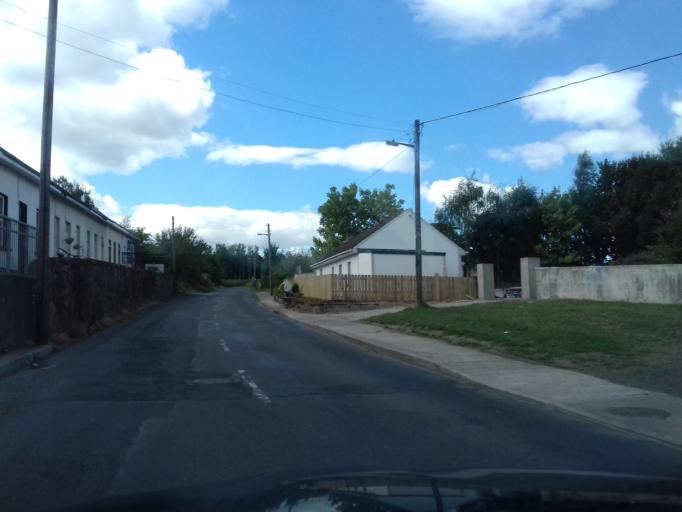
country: IE
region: Munster
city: Carrick-on-Suir
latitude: 52.3519
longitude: -7.4199
